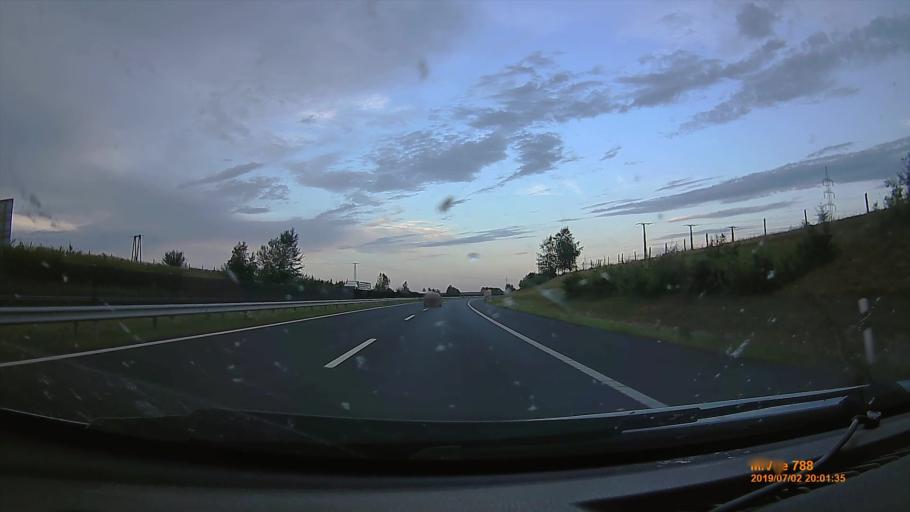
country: HU
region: Zala
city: Nagykanizsa
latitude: 46.4784
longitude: 16.9960
